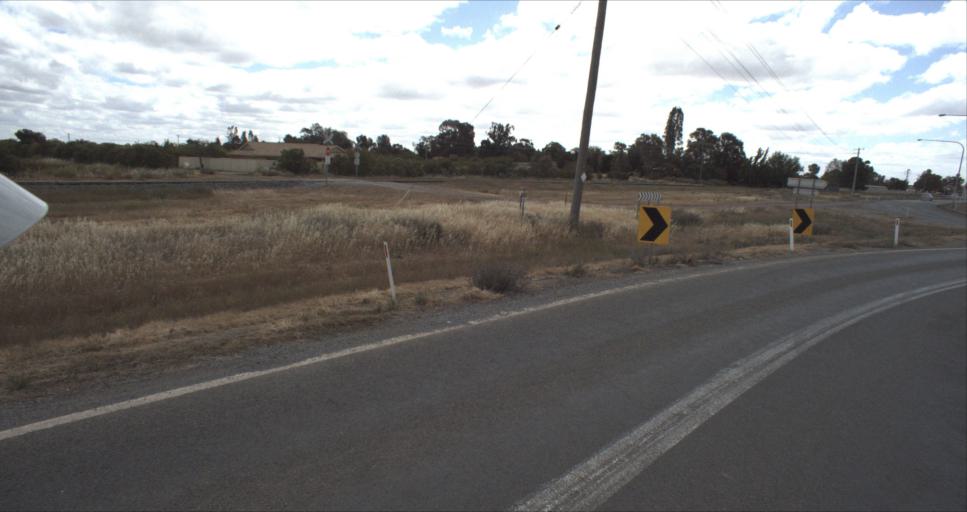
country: AU
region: New South Wales
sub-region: Leeton
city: Leeton
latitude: -34.5718
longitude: 146.3945
